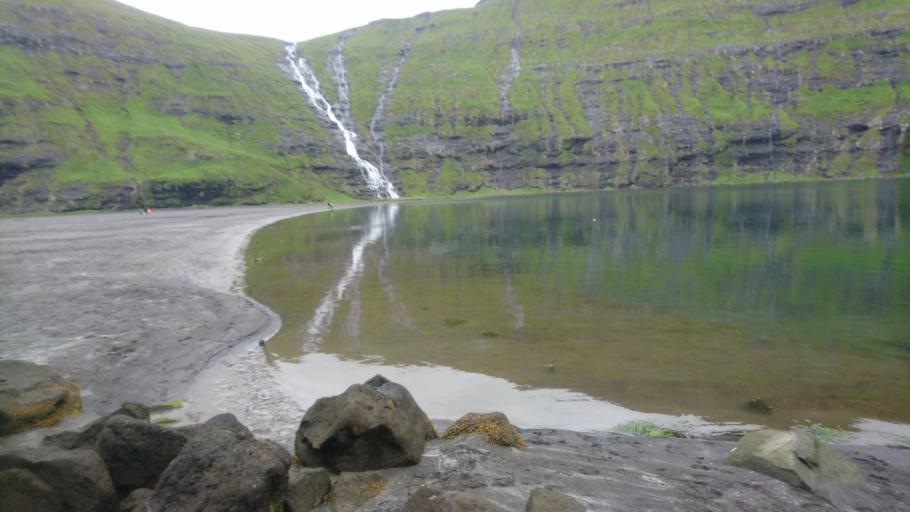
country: FO
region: Streymoy
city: Vestmanna
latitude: 62.2467
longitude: -7.1911
